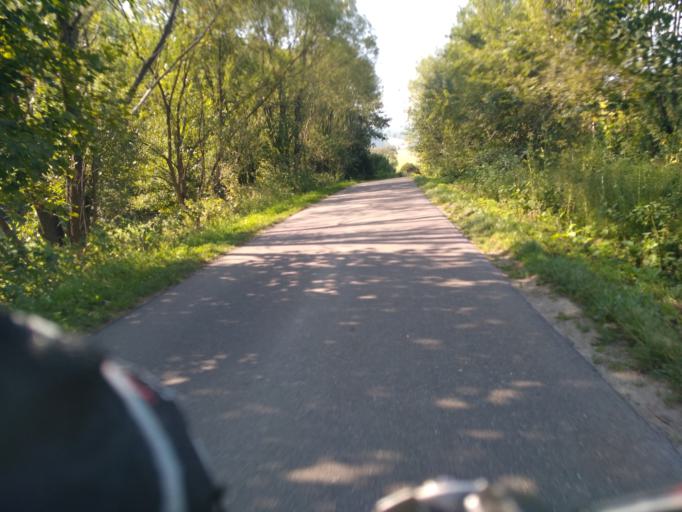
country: PL
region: Subcarpathian Voivodeship
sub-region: Powiat brzozowski
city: Golcowa
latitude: 49.7832
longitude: 22.0149
